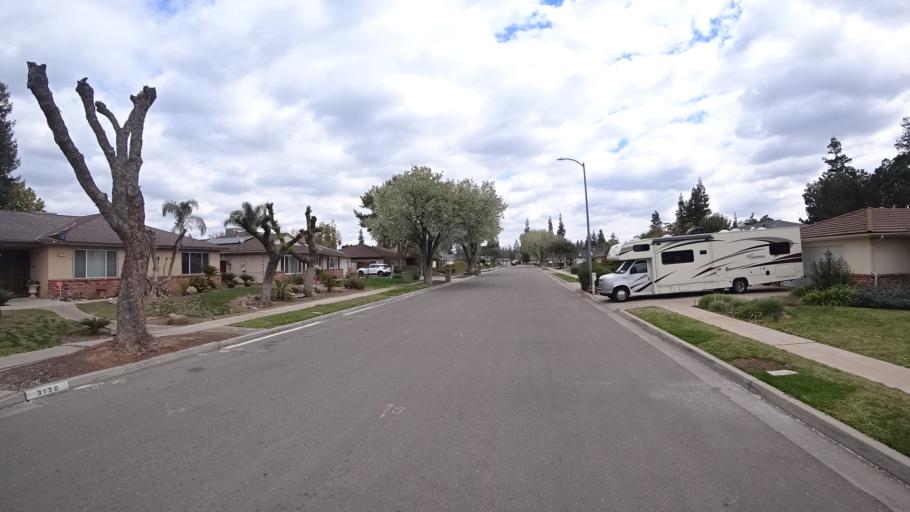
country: US
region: California
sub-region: Fresno County
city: Fresno
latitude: 36.8183
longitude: -119.8472
